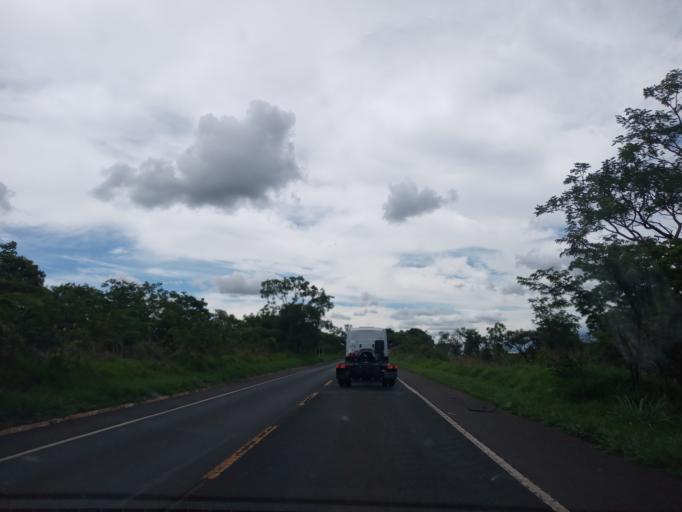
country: BR
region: Minas Gerais
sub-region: Uberlandia
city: Uberlandia
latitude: -19.1832
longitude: -47.8781
